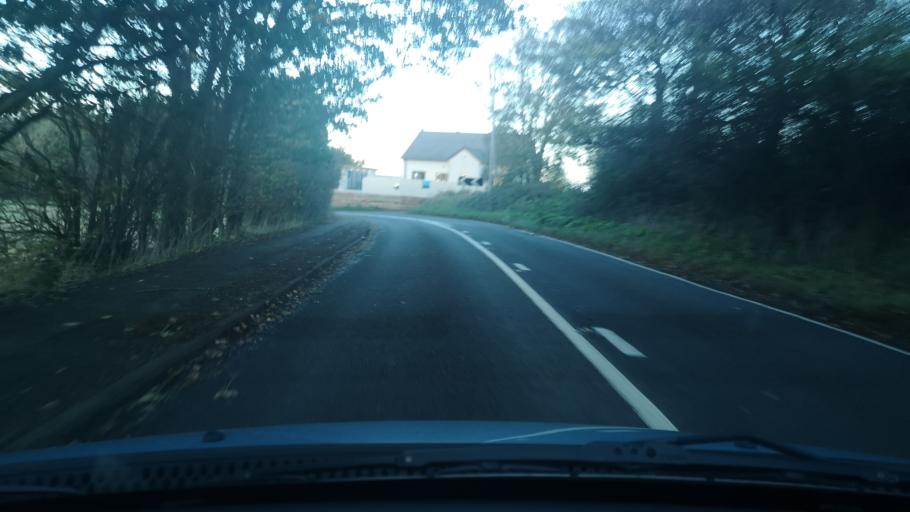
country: GB
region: England
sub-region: City and Borough of Wakefield
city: Middlestown
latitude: 53.6366
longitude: -1.5852
